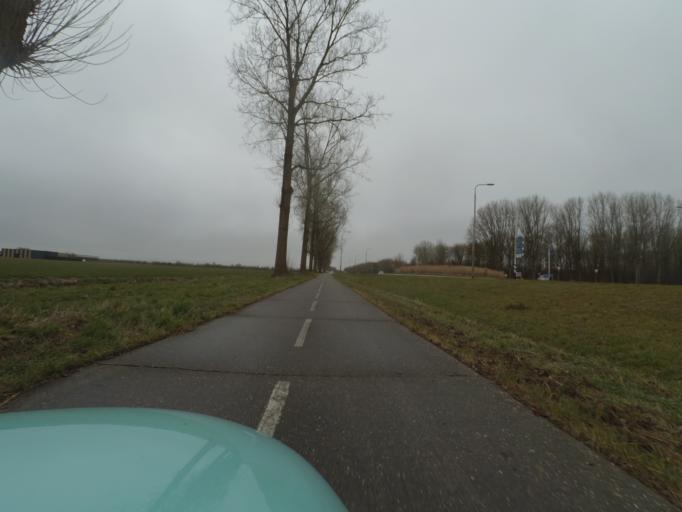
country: NL
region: Flevoland
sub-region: Gemeente Dronten
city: Dronten
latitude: 52.5250
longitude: 5.7361
